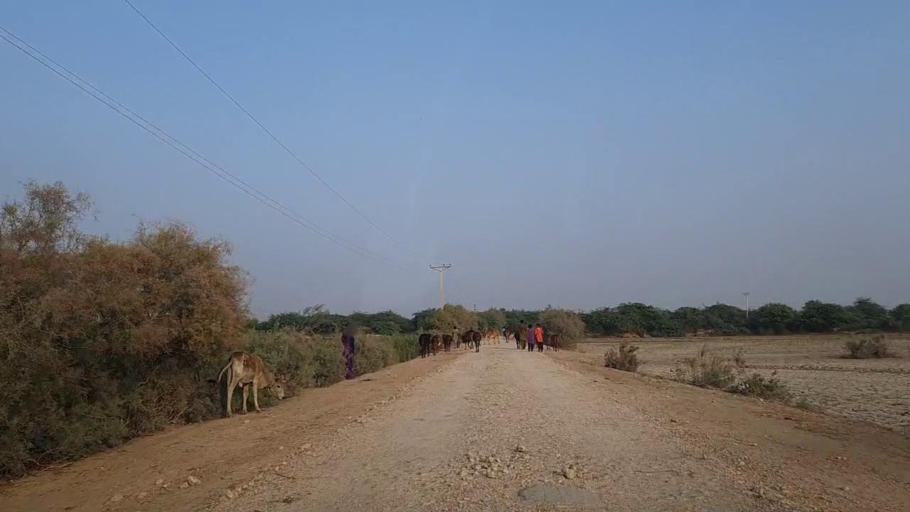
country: PK
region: Sindh
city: Thatta
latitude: 24.6920
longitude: 67.8075
